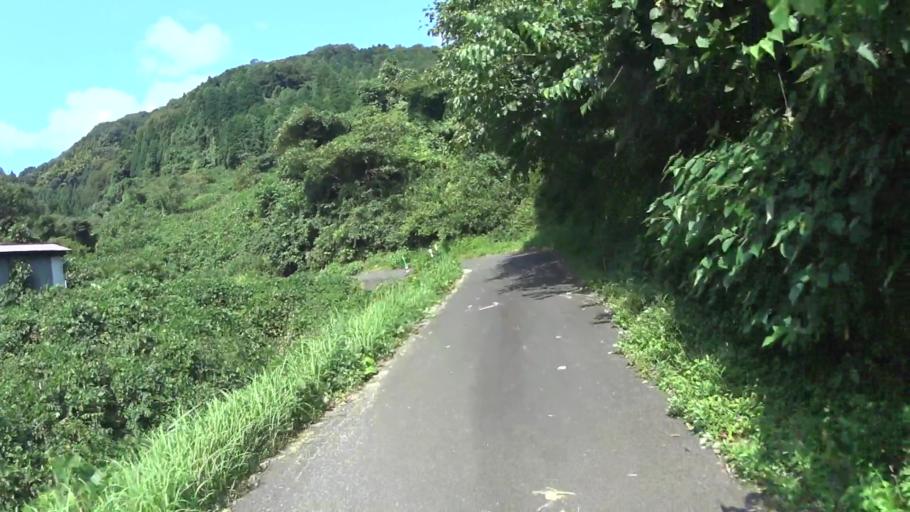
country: JP
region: Kyoto
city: Miyazu
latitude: 35.6571
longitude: 135.2444
